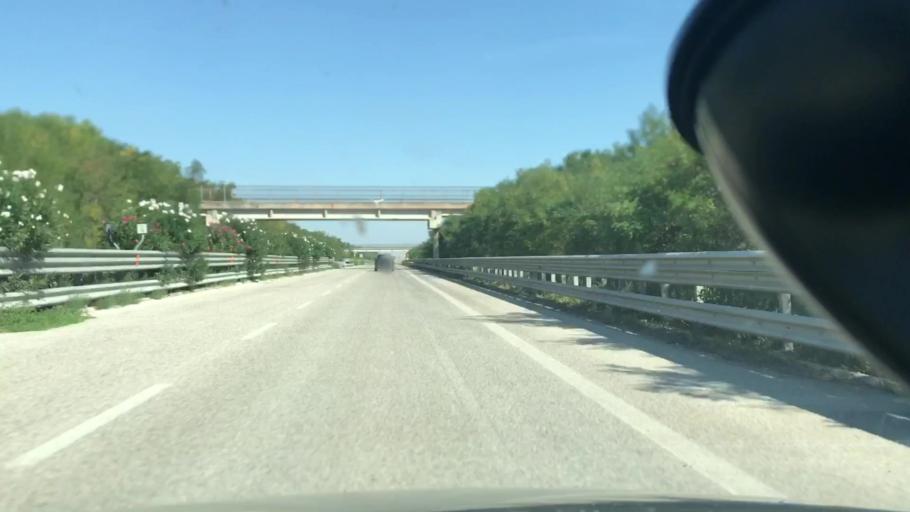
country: IT
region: Apulia
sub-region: Provincia di Foggia
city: Ordona
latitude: 41.2883
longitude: 15.5540
